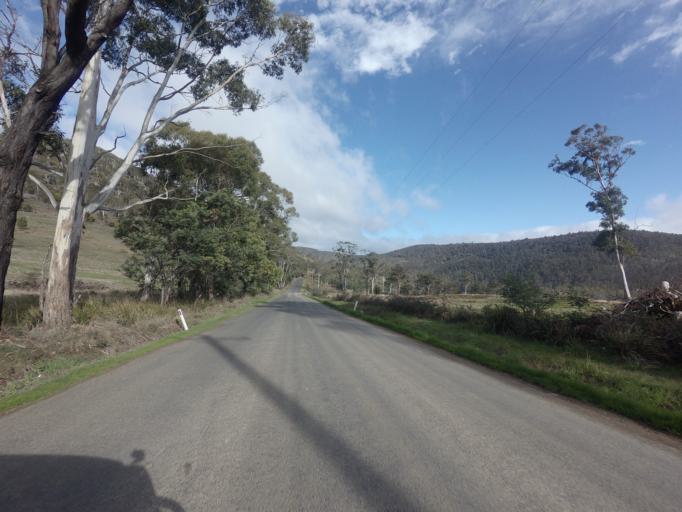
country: AU
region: Tasmania
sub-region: Derwent Valley
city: New Norfolk
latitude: -42.7782
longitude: 146.9639
